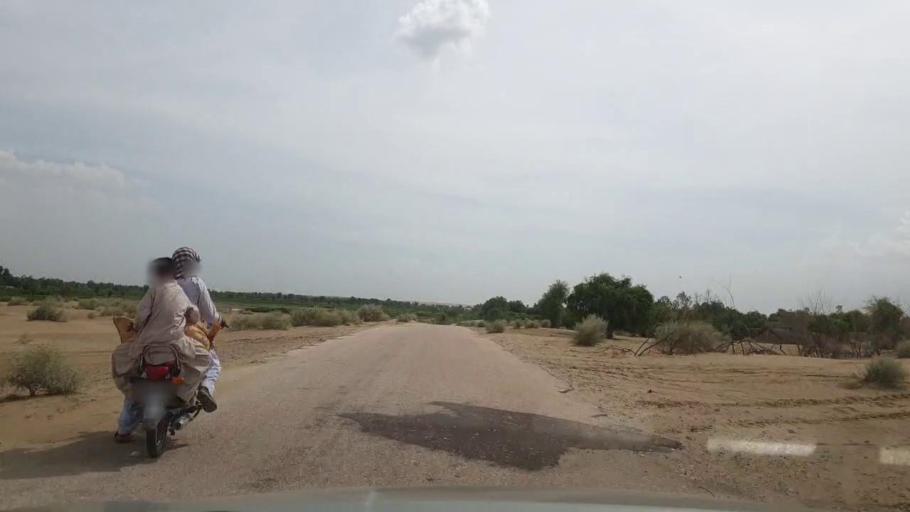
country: PK
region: Sindh
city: Kot Diji
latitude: 27.1499
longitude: 69.0320
